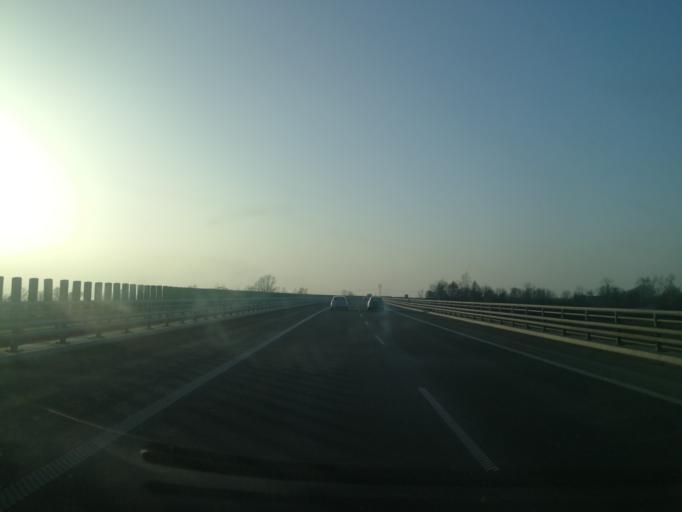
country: PL
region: Warmian-Masurian Voivodeship
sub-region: Powiat elblaski
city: Gronowo Elblaskie
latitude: 54.1651
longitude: 19.2467
